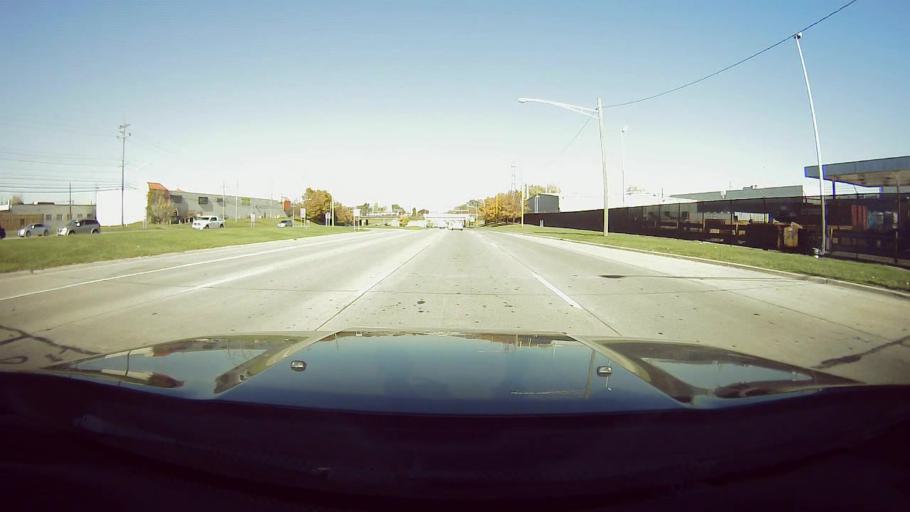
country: US
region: Michigan
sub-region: Wayne County
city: Redford
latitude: 42.3738
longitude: -83.2753
